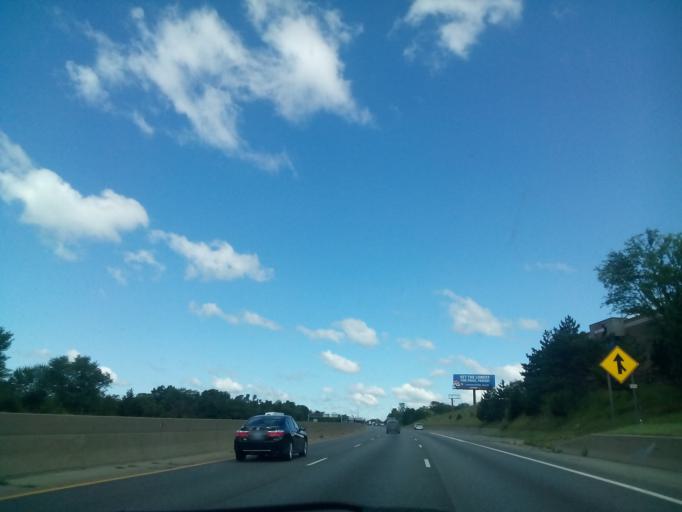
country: US
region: Michigan
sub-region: Genesee County
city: Flint
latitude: 42.9903
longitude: -83.7393
